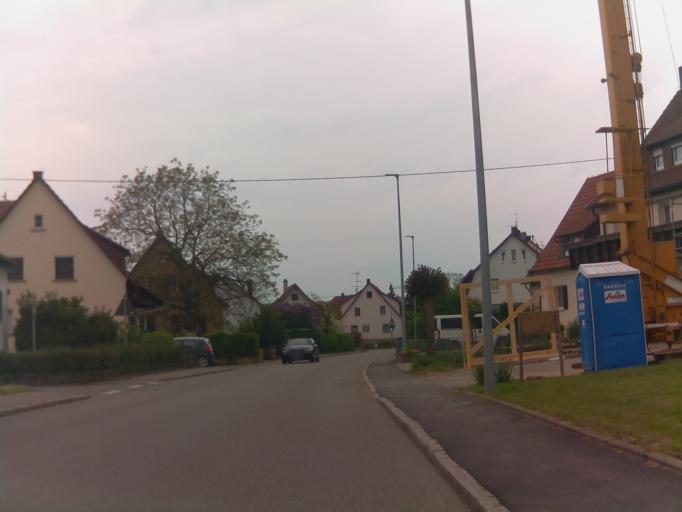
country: DE
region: Baden-Wuerttemberg
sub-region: Tuebingen Region
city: Pliezhausen
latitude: 48.5739
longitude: 9.1852
